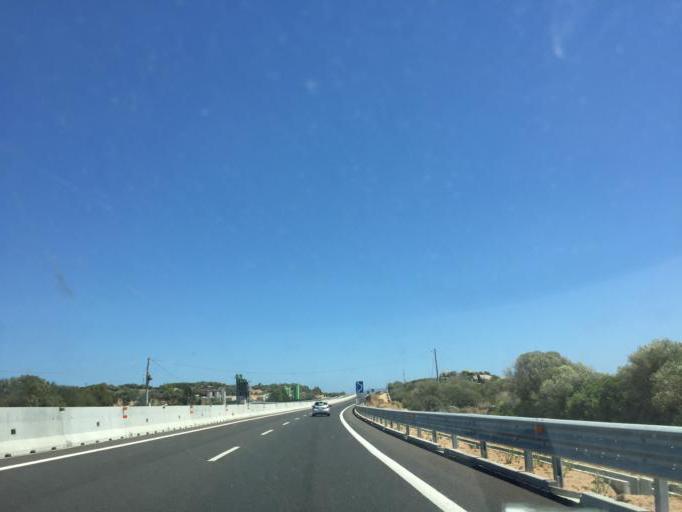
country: IT
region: Sardinia
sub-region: Provincia di Olbia-Tempio
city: Loiri Porto San Paolo
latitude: 40.8805
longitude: 9.4672
